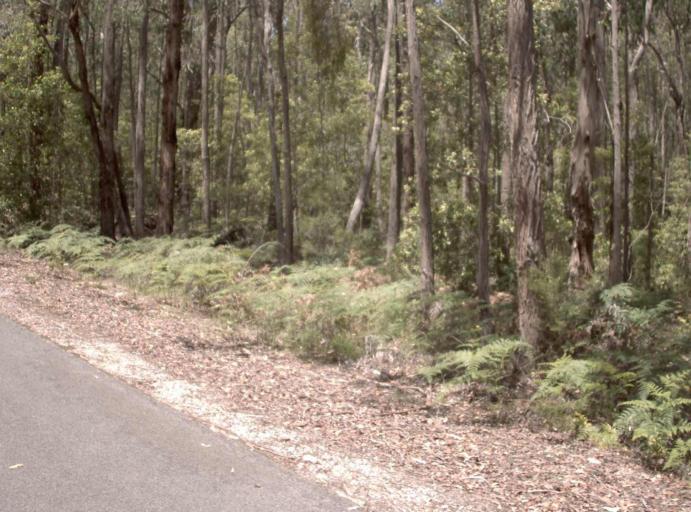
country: AU
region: New South Wales
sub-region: Bombala
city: Bombala
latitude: -37.4870
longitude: 148.9300
